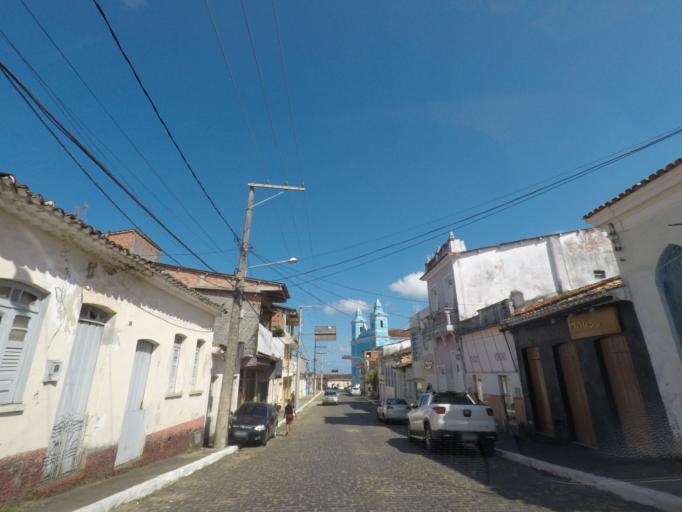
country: BR
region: Bahia
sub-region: Camamu
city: Camamu
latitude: -13.9455
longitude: -39.1049
